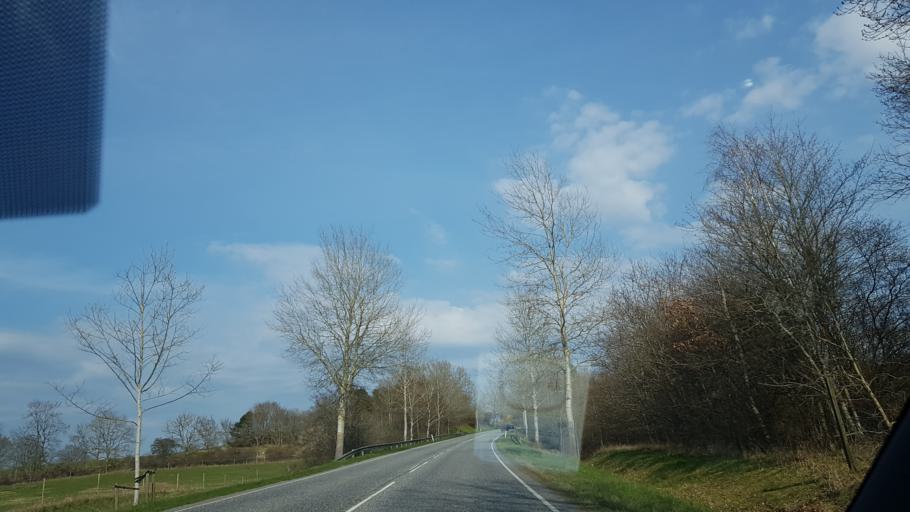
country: DK
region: Capital Region
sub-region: Frederikssund Kommune
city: Slangerup
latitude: 55.8395
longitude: 12.1973
